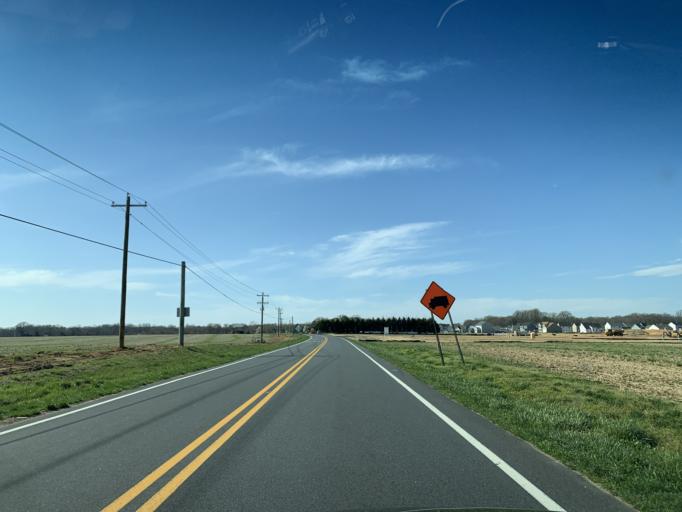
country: US
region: Delaware
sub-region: Kent County
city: Riverview
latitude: 38.9793
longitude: -75.5014
